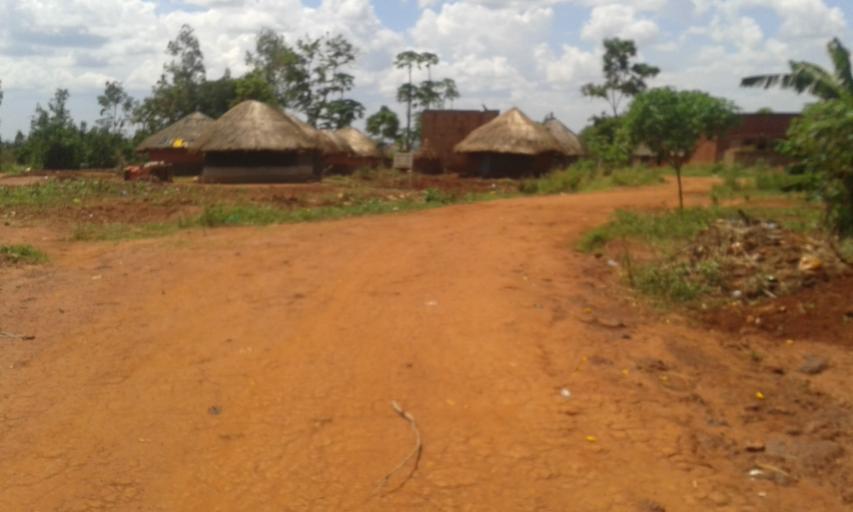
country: UG
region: Northern Region
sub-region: Gulu District
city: Gulu
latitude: 2.7910
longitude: 32.3201
